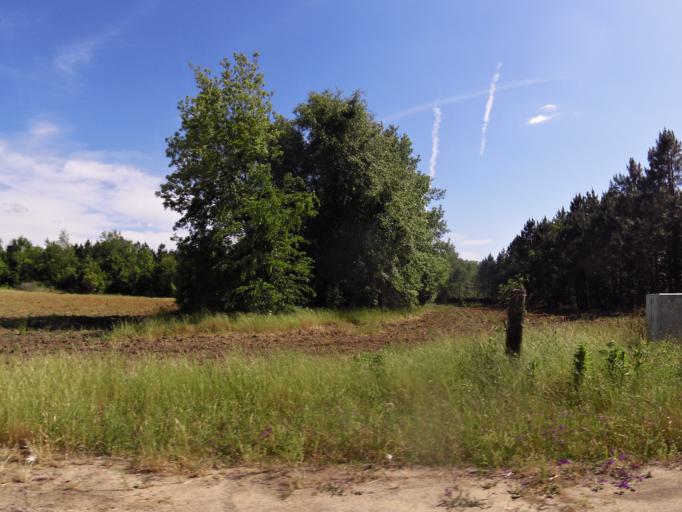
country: US
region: South Carolina
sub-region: Barnwell County
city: Blackville
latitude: 33.3486
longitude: -81.2160
